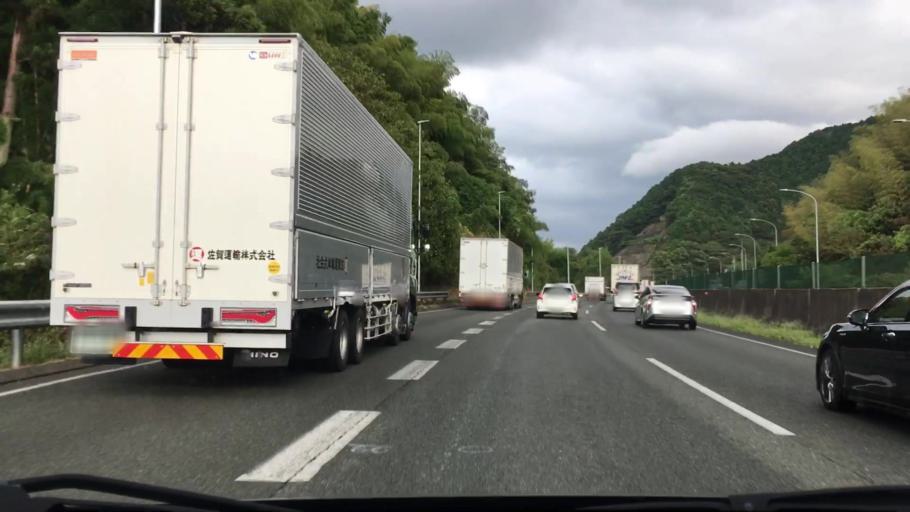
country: JP
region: Fukuoka
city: Nishifukuma
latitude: 33.7501
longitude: 130.5467
